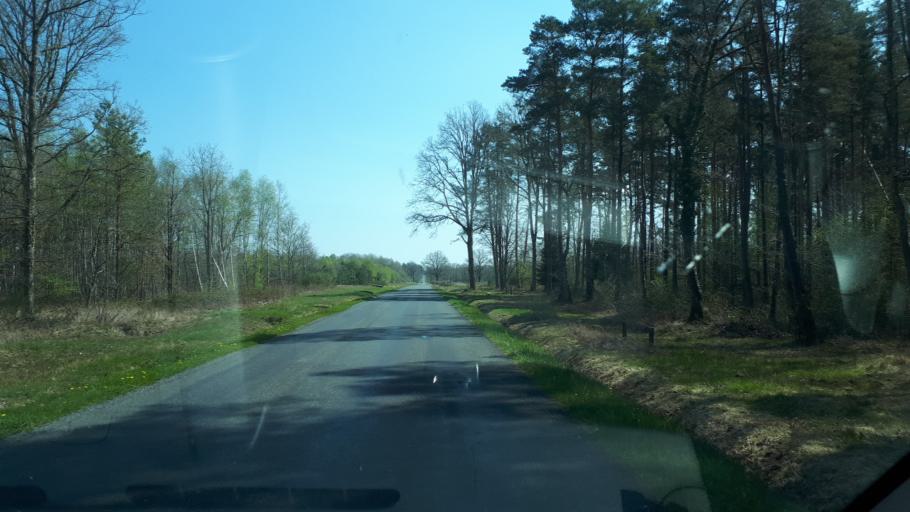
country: FR
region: Centre
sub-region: Departement du Cher
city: Neuvy-sur-Barangeon
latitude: 47.3182
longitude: 2.1536
